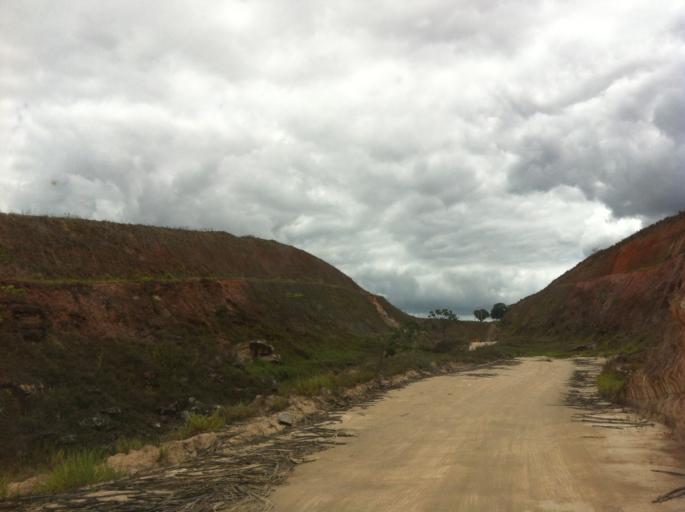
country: BR
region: Alagoas
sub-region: Novo Lino
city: Novo Lino
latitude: -8.8835
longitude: -35.6308
